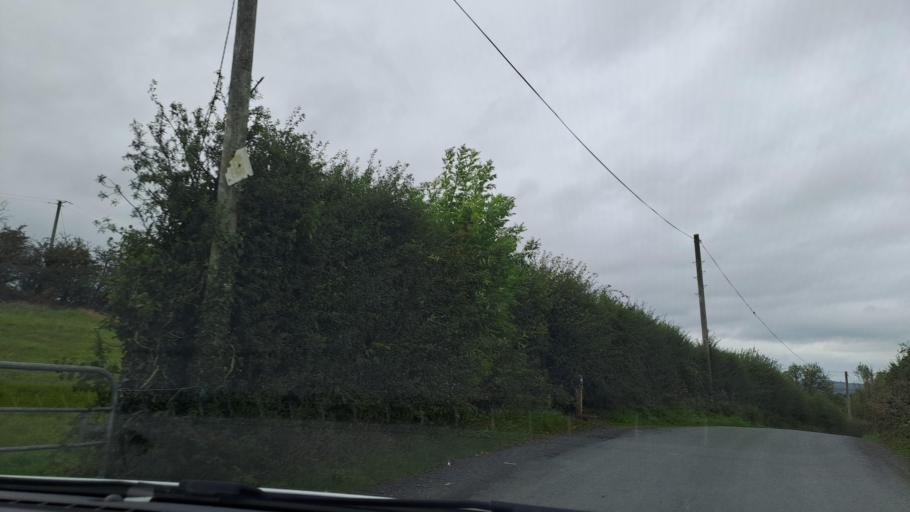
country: IE
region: Ulster
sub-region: An Cabhan
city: Kingscourt
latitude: 54.0146
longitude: -6.8606
